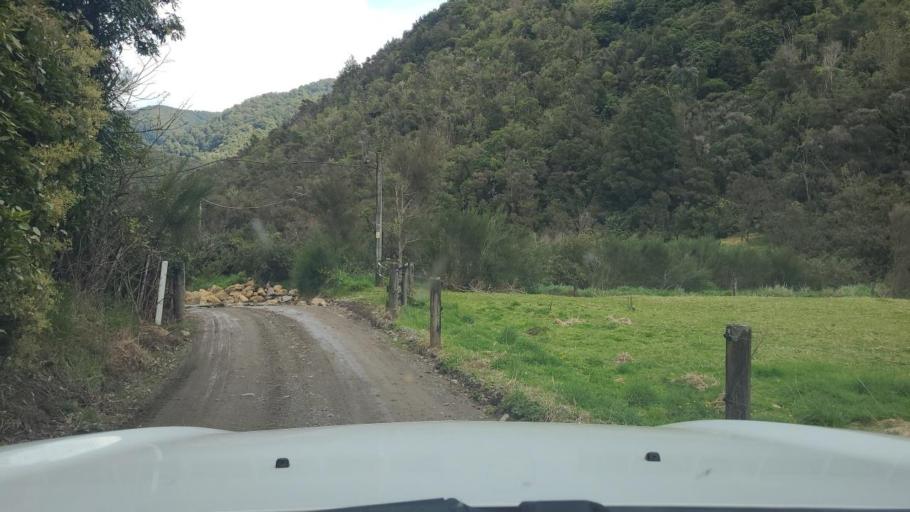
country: NZ
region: Wellington
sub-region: Masterton District
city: Masterton
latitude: -40.9477
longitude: 175.4554
